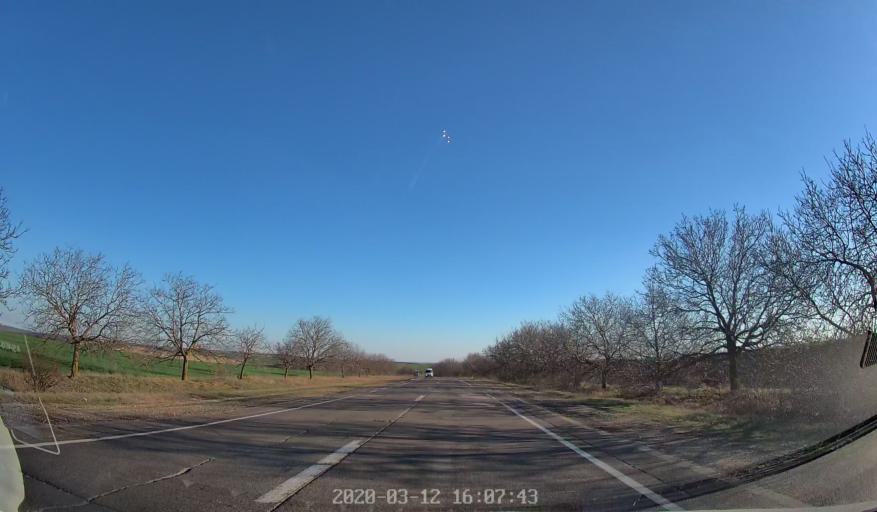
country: MD
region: Anenii Noi
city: Anenii Noi
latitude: 46.9761
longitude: 29.1980
